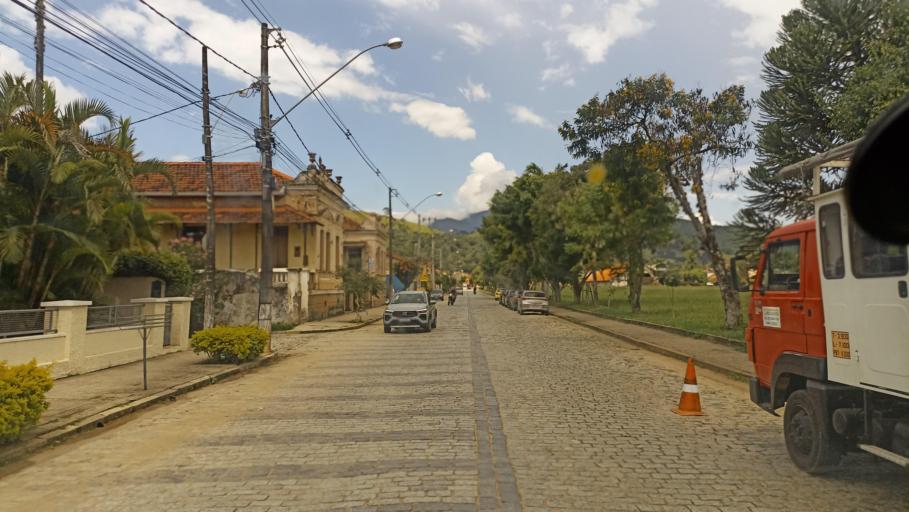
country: BR
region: Minas Gerais
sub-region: Passa Quatro
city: Passa Quatro
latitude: -22.3876
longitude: -44.9654
